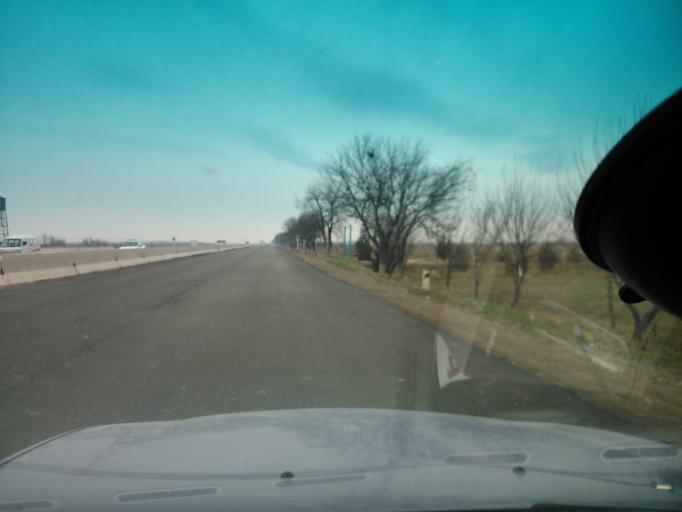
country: UZ
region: Sirdaryo
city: Guliston
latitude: 40.4319
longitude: 68.7810
